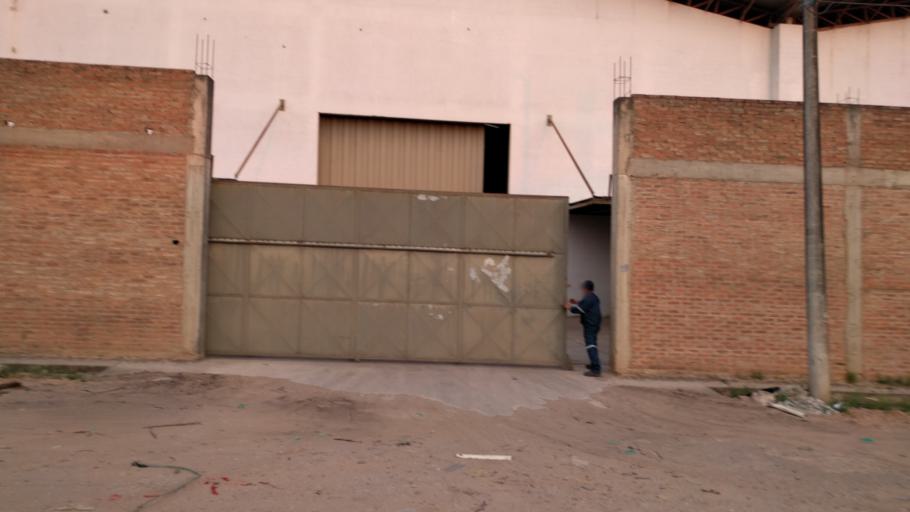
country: BO
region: Santa Cruz
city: Santa Cruz de la Sierra
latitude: -17.7569
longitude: -63.1468
